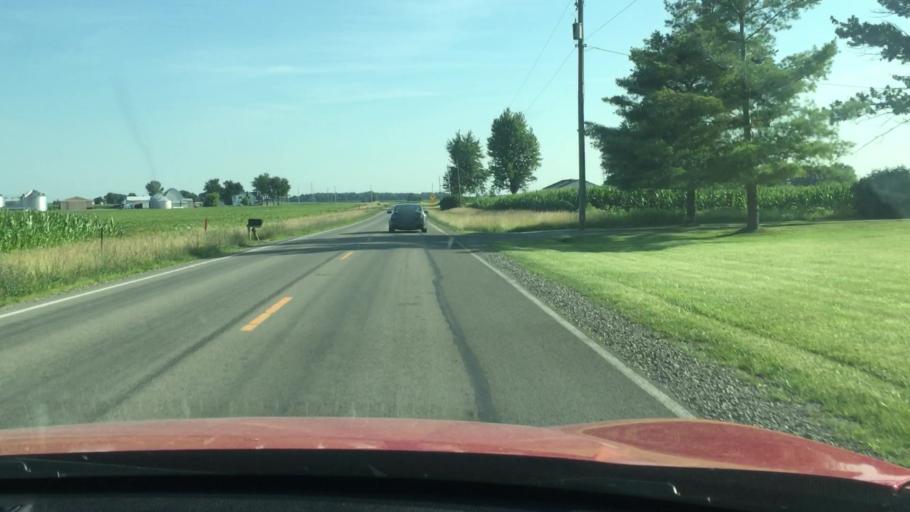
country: US
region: Ohio
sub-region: Hardin County
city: Ada
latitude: 40.6969
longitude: -83.8549
